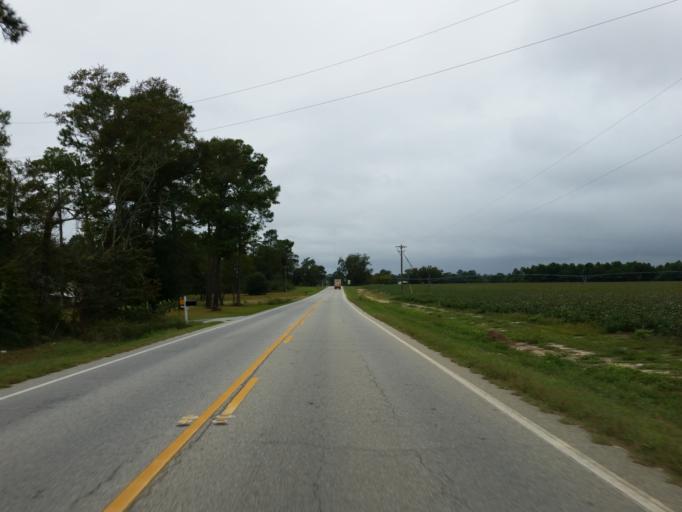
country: US
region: Georgia
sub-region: Cook County
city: Adel
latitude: 31.1334
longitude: -83.3768
